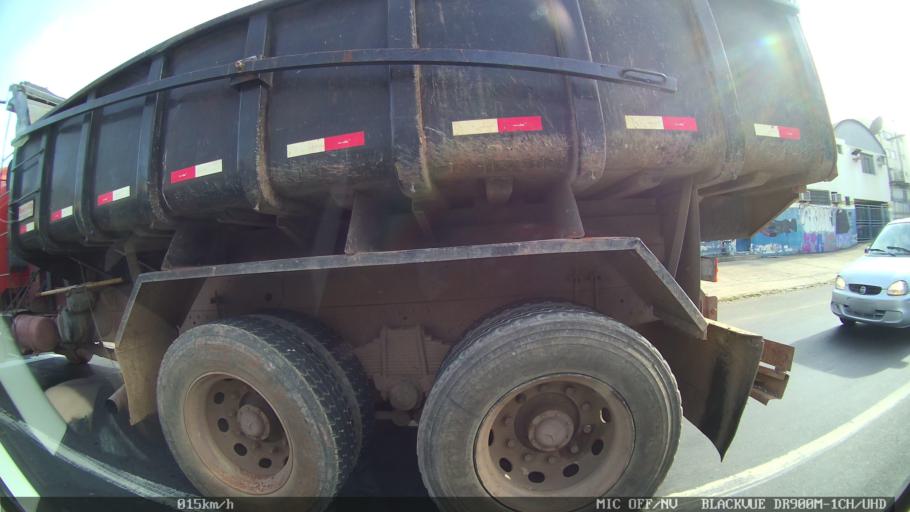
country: BR
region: Sao Paulo
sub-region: Piracicaba
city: Piracicaba
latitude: -22.7045
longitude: -47.6556
